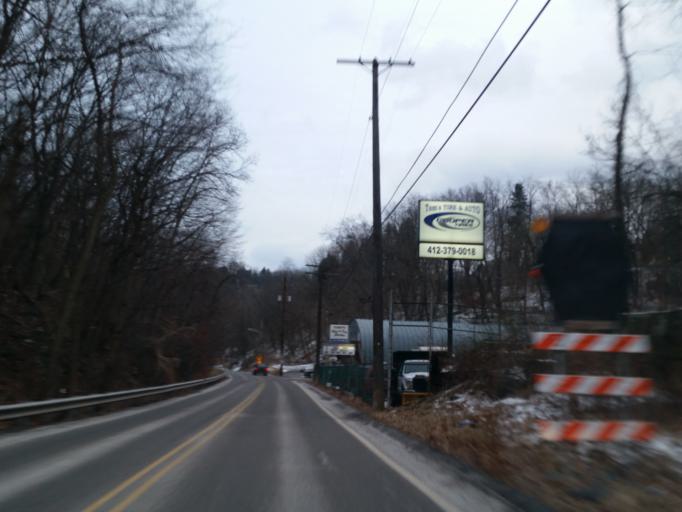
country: US
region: Pennsylvania
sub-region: Allegheny County
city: Brentwood
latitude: 40.3907
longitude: -79.9600
